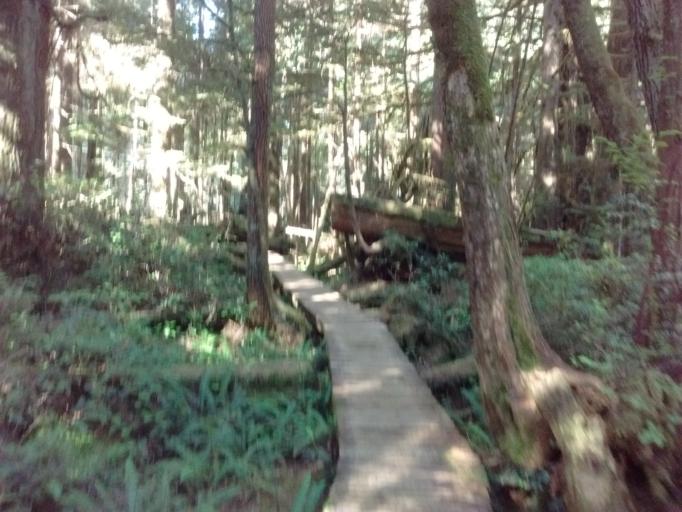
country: CA
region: British Columbia
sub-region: Regional District of Alberni-Clayoquot
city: Ucluelet
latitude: 49.0432
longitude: -125.6820
